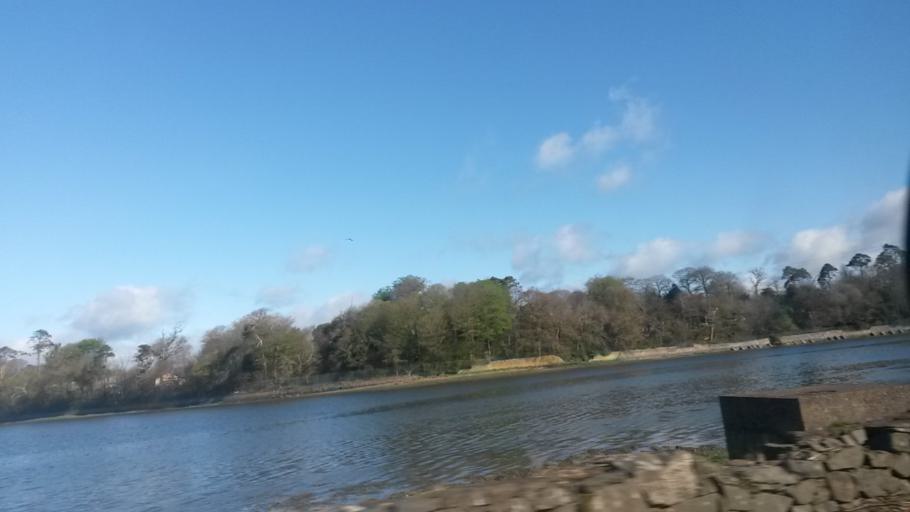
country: IE
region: Munster
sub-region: County Cork
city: Cobh
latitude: 51.8873
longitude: -8.3086
